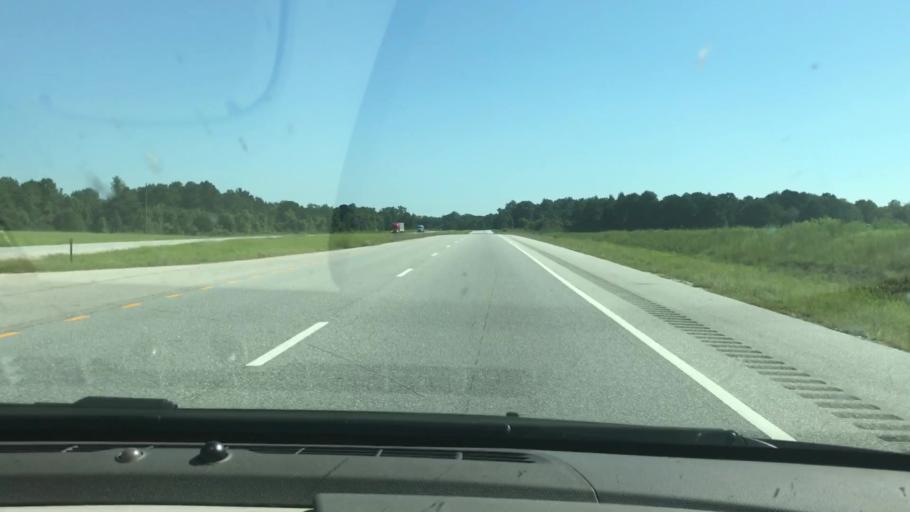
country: US
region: Alabama
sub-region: Russell County
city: Ladonia
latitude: 32.3614
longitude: -85.1039
